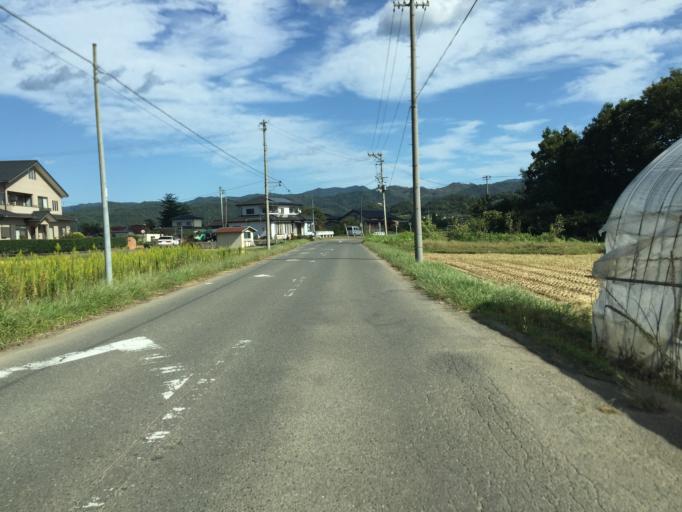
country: JP
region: Fukushima
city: Yanagawamachi-saiwaicho
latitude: 37.8407
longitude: 140.5899
